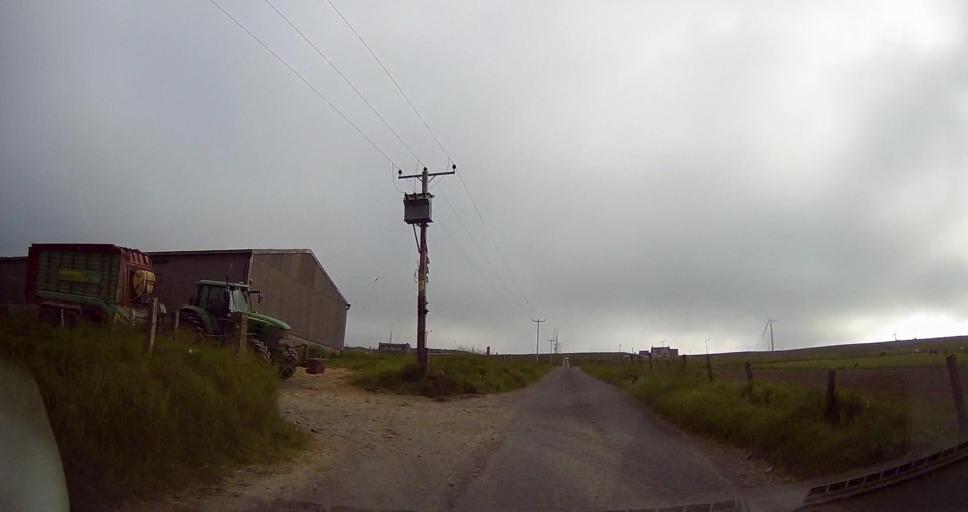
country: GB
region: Scotland
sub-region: Orkney Islands
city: Orkney
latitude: 59.1192
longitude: -3.1280
